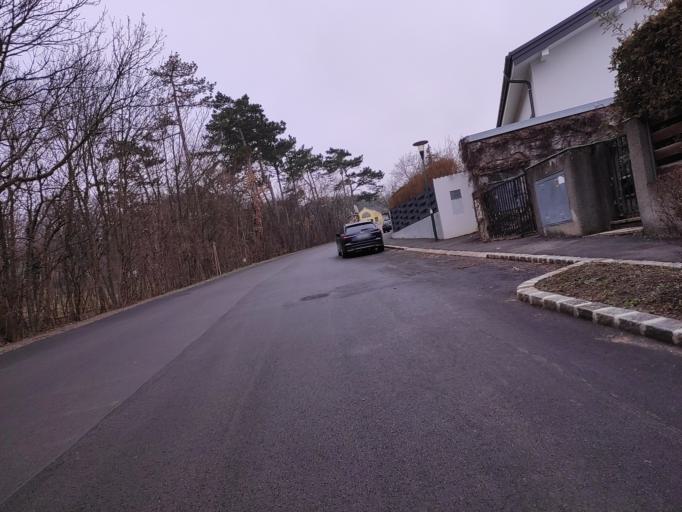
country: AT
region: Lower Austria
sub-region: Politischer Bezirk Modling
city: Perchtoldsdorf
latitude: 48.1048
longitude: 16.2644
